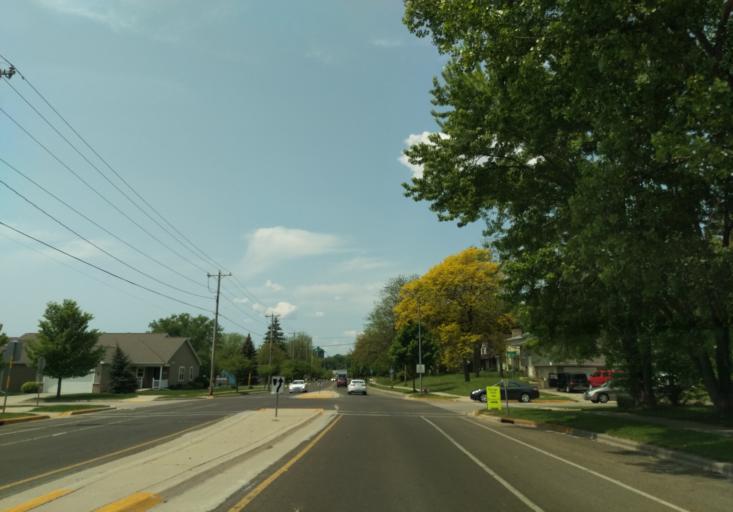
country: US
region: Wisconsin
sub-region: Dane County
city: Monona
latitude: 43.0733
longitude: -89.3015
